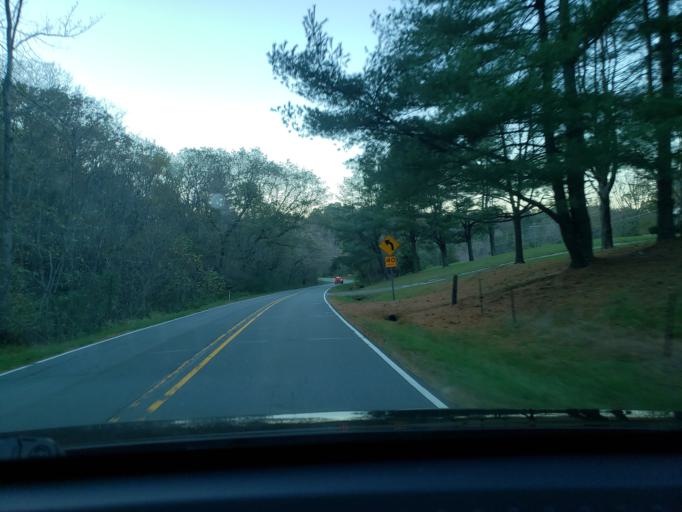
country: US
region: North Carolina
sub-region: Stokes County
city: Danbury
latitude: 36.4144
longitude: -80.2231
